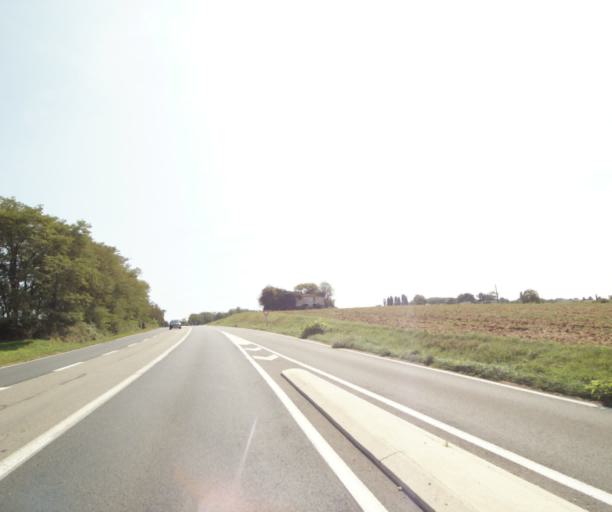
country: FR
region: Bourgogne
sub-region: Departement de Saone-et-Loire
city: Tournus
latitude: 46.5493
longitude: 4.9176
